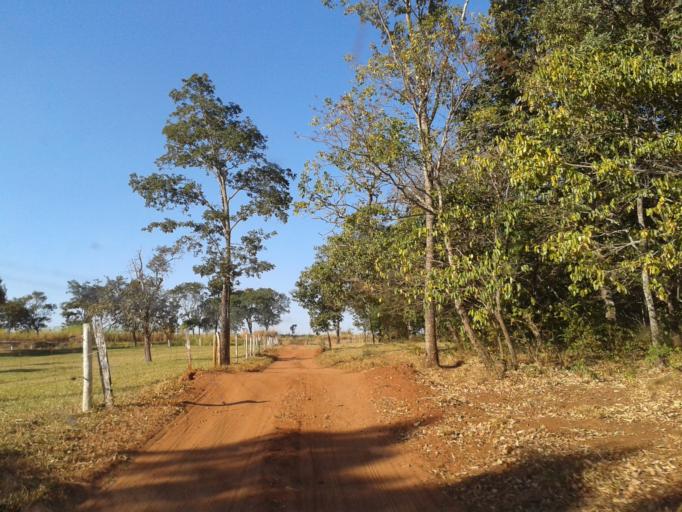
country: BR
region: Minas Gerais
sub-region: Capinopolis
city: Capinopolis
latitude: -18.7576
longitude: -49.5370
